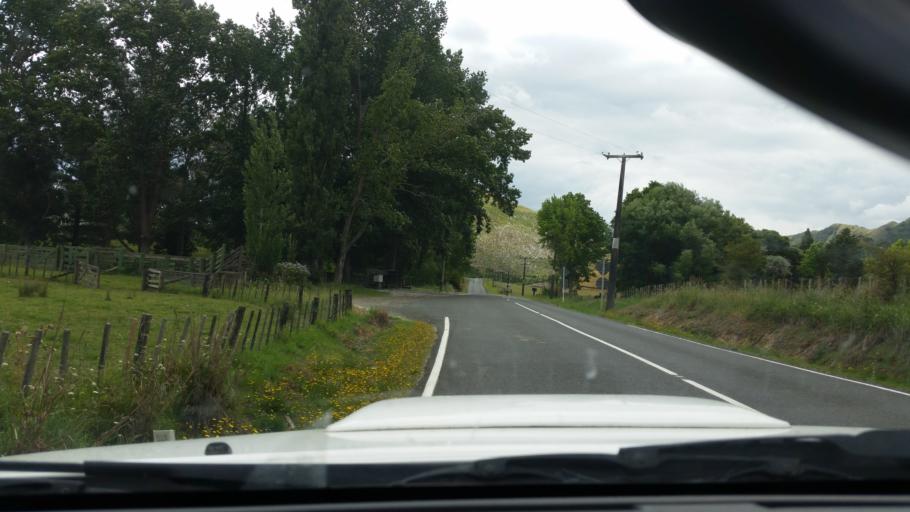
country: NZ
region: Northland
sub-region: Kaipara District
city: Dargaville
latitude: -35.7458
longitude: 173.8774
